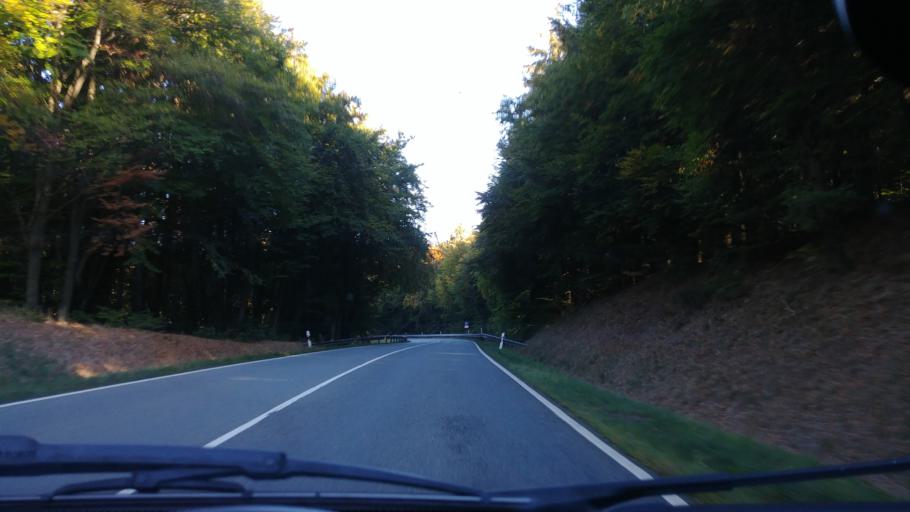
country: DE
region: Rheinland-Pfalz
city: Rettert
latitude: 50.2034
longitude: 7.9525
